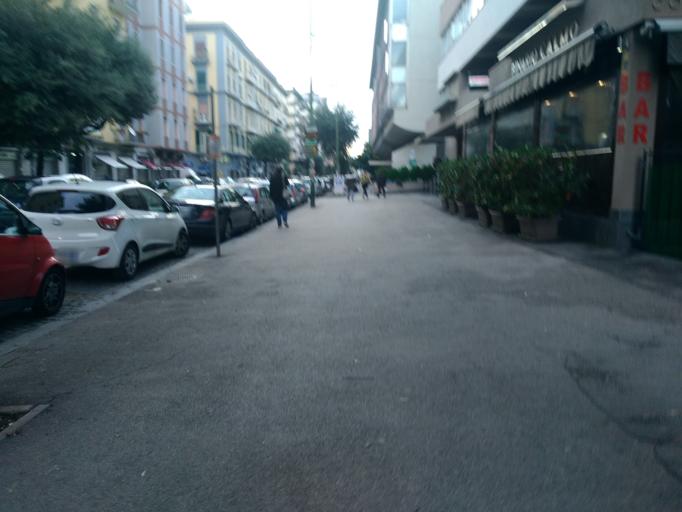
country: IT
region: Campania
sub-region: Provincia di Napoli
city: Napoli
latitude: 40.8544
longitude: 14.2735
